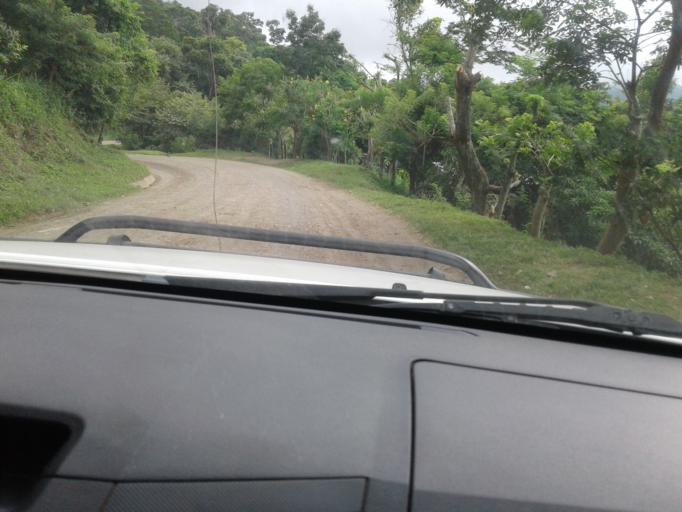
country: NI
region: Matagalpa
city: San Ramon
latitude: 12.9077
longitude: -85.7996
